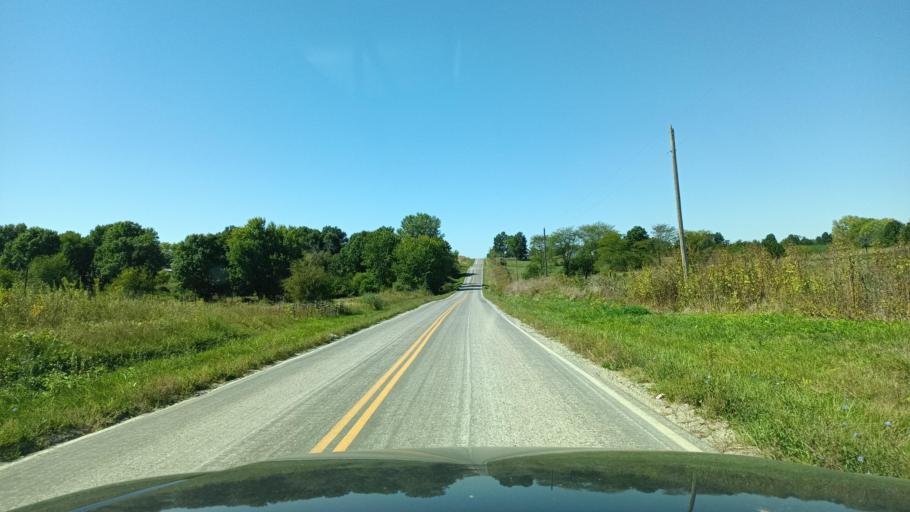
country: US
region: Missouri
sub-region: Macon County
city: La Plata
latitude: 40.0225
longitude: -92.5669
